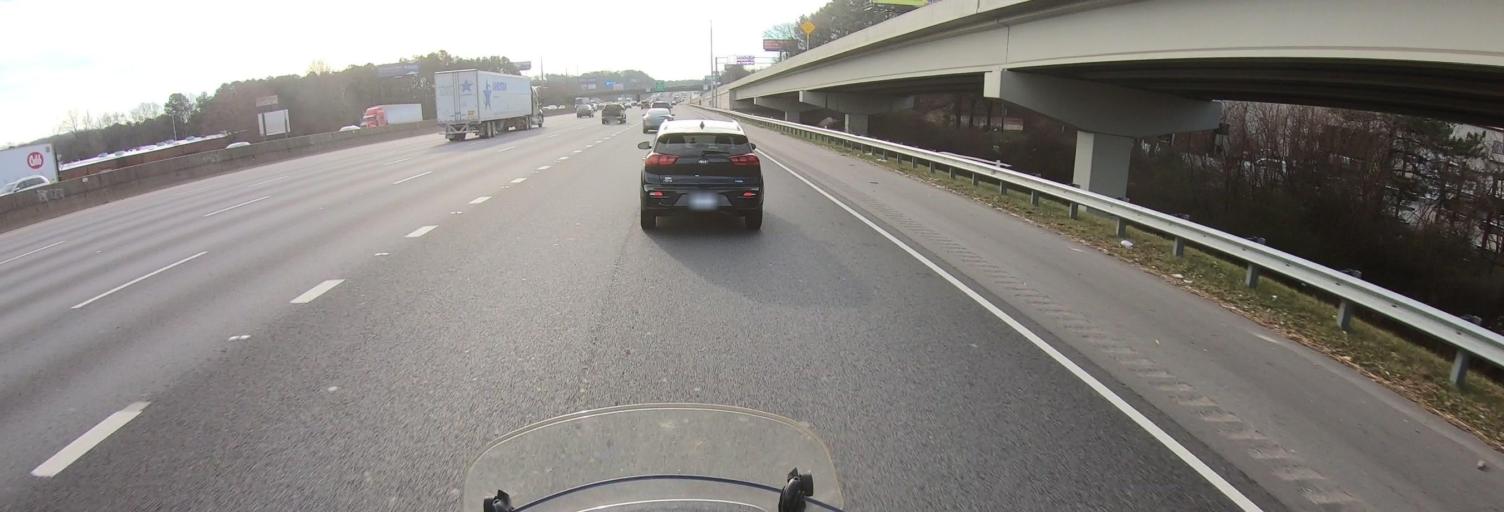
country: US
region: Georgia
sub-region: Cobb County
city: Marietta
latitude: 33.9739
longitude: -84.5350
